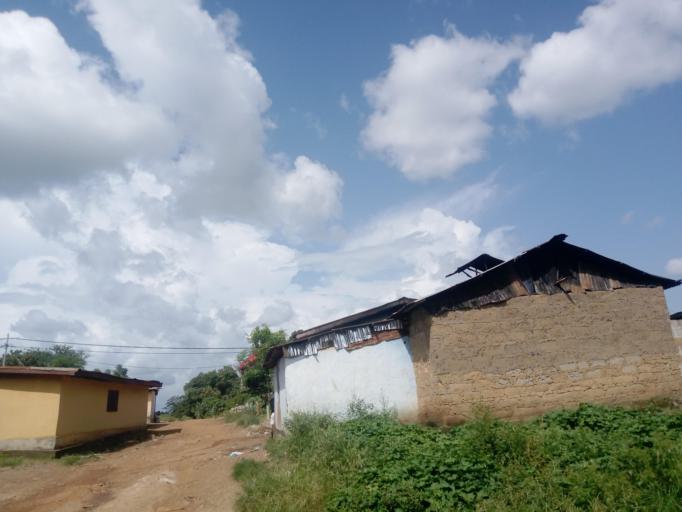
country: SL
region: Northern Province
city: Makeni
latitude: 8.9000
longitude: -12.0432
